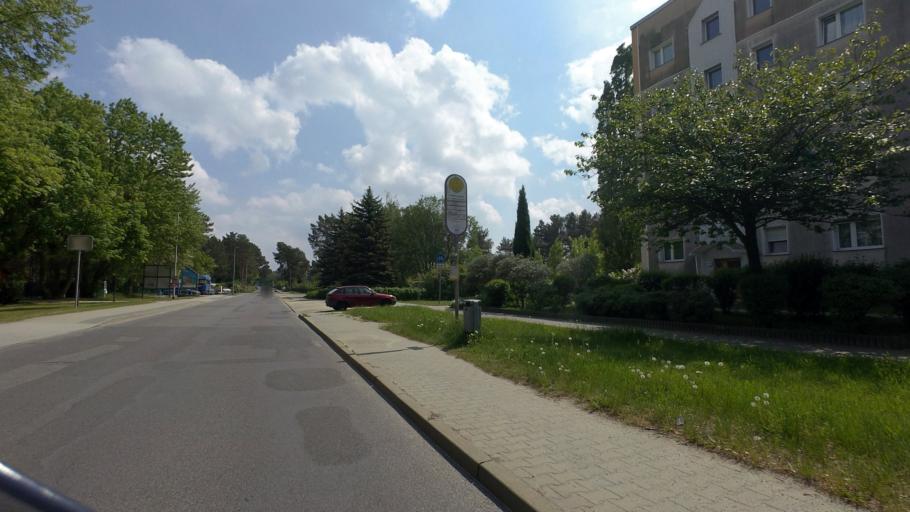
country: DE
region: Saxony
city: Weisswasser
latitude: 51.4963
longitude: 14.6447
